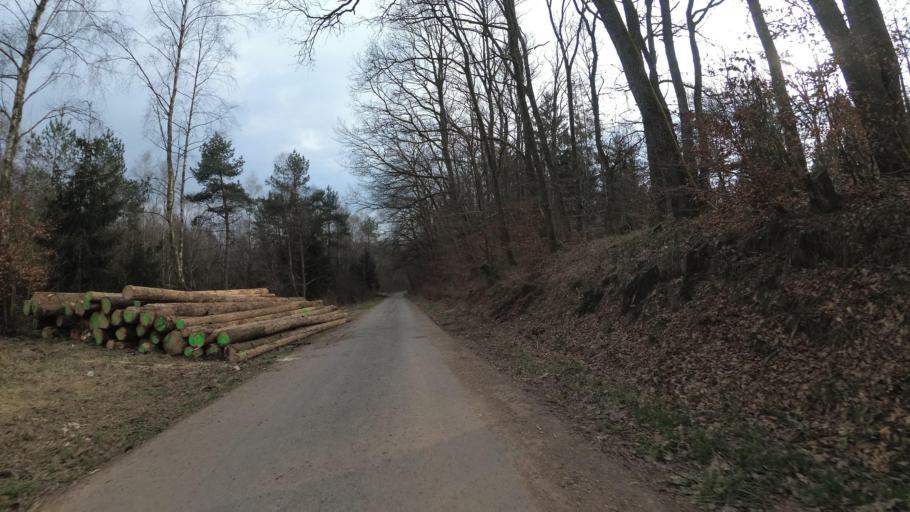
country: DE
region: Rheinland-Pfalz
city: Gimbweiler
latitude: 49.5813
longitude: 7.1755
